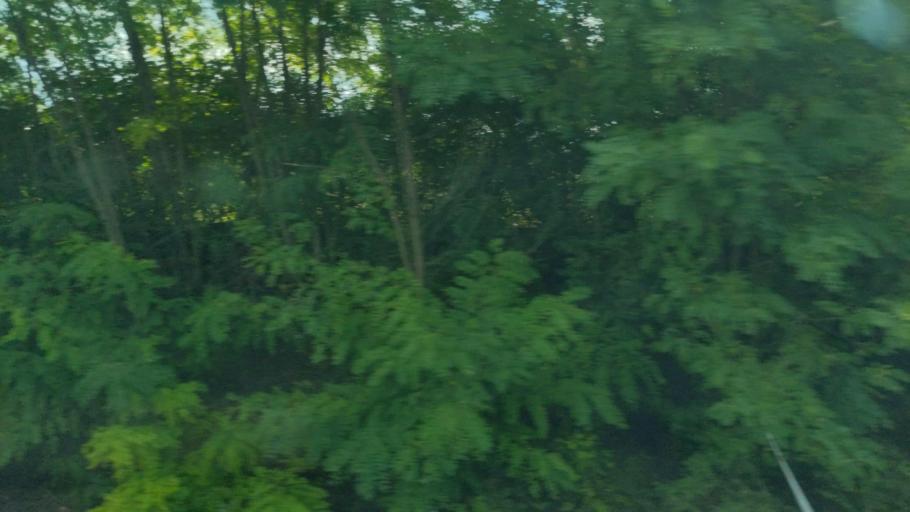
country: CZ
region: Central Bohemia
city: Cesky Brod
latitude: 50.0819
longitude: 14.8842
